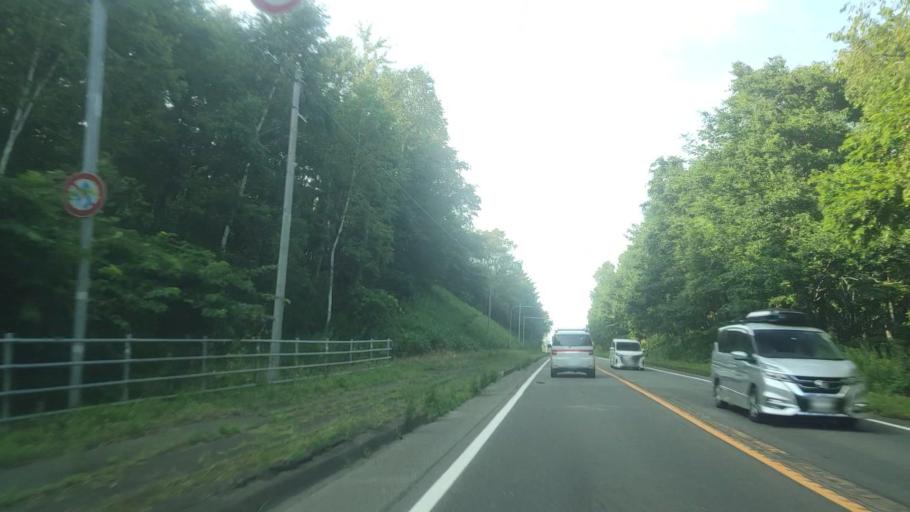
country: JP
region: Hokkaido
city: Chitose
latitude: 42.8637
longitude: 141.8225
